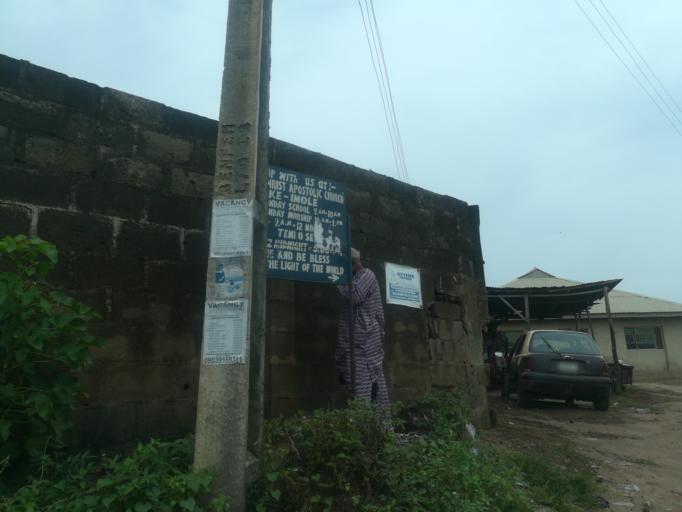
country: NG
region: Oyo
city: Egbeda
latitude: 7.3807
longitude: 3.9962
